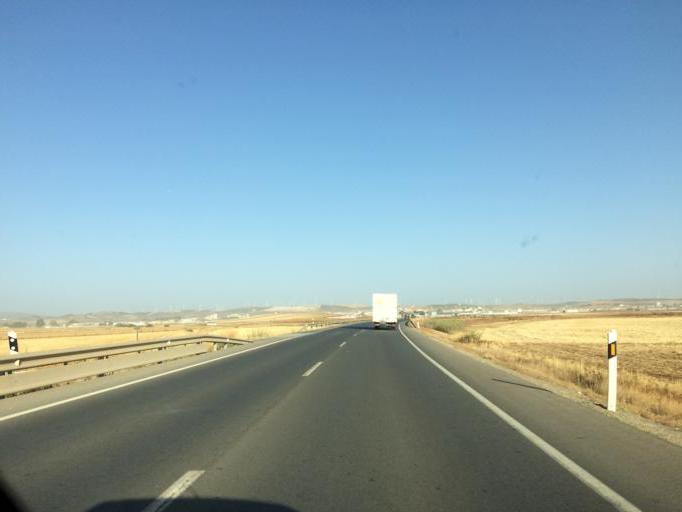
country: ES
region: Andalusia
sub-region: Provincia de Malaga
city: Campillos
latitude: 37.0478
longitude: -4.8365
